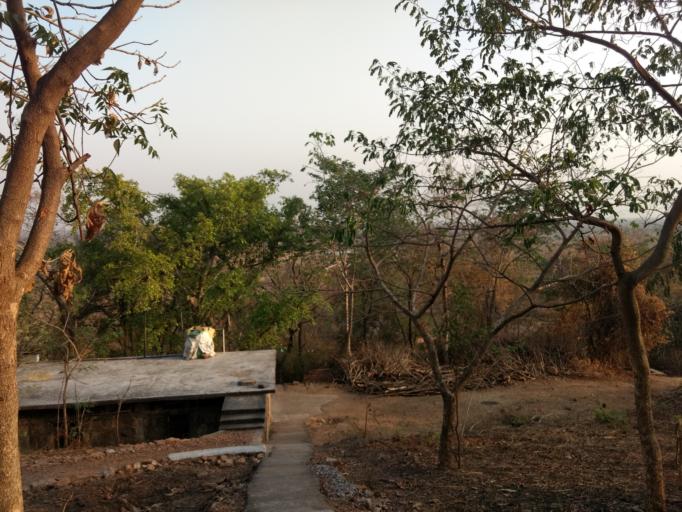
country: IN
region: Maharashtra
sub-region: Bhandara
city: Pauni
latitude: 20.5863
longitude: 79.7841
